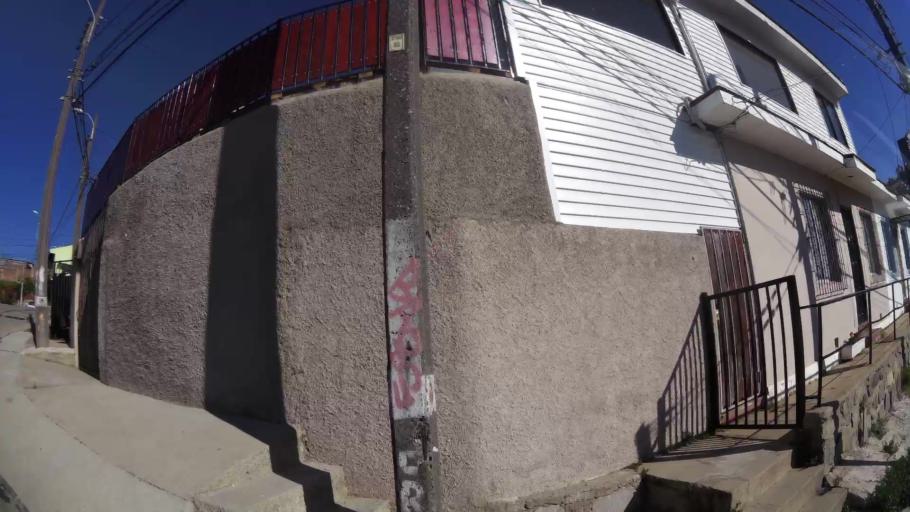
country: CL
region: Valparaiso
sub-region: Provincia de Valparaiso
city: Valparaiso
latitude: -33.0543
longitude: -71.6198
